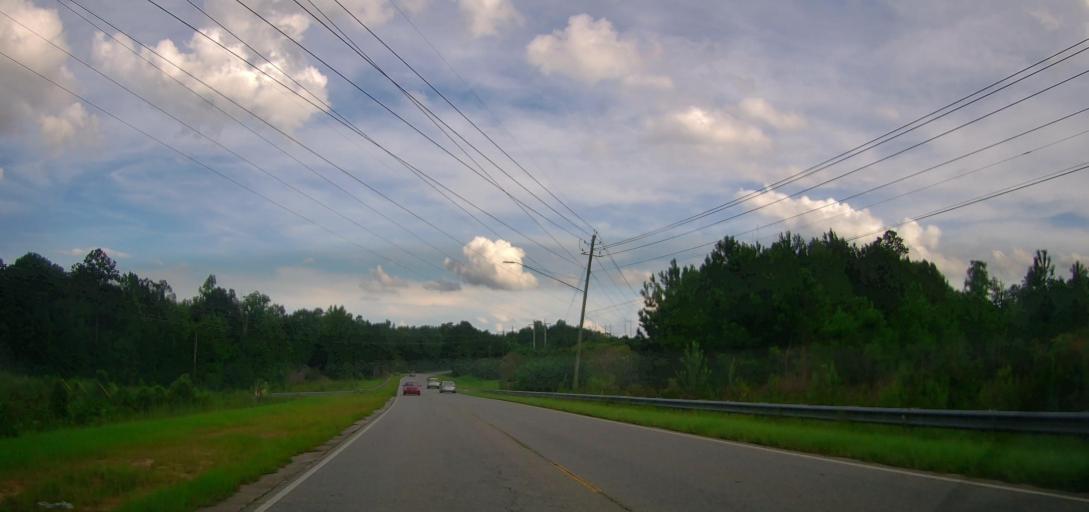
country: US
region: Alabama
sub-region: Russell County
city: Phenix City
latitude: 32.5175
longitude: -85.0158
